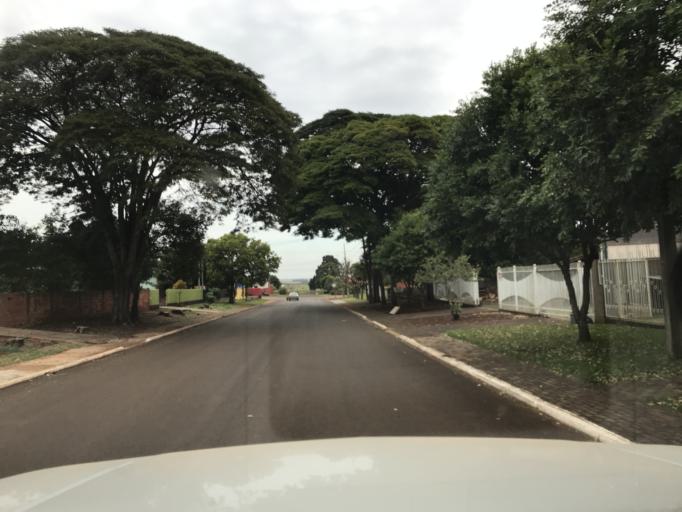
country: BR
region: Parana
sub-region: Marechal Candido Rondon
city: Marechal Candido Rondon
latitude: -24.4680
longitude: -53.9584
